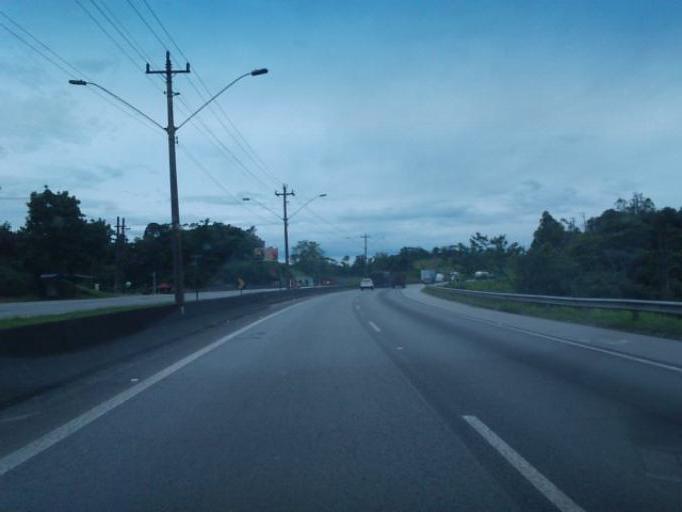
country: BR
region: Sao Paulo
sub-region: Sao Lourenco Da Serra
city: Sao Lourenco da Serra
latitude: -23.8644
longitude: -46.9488
